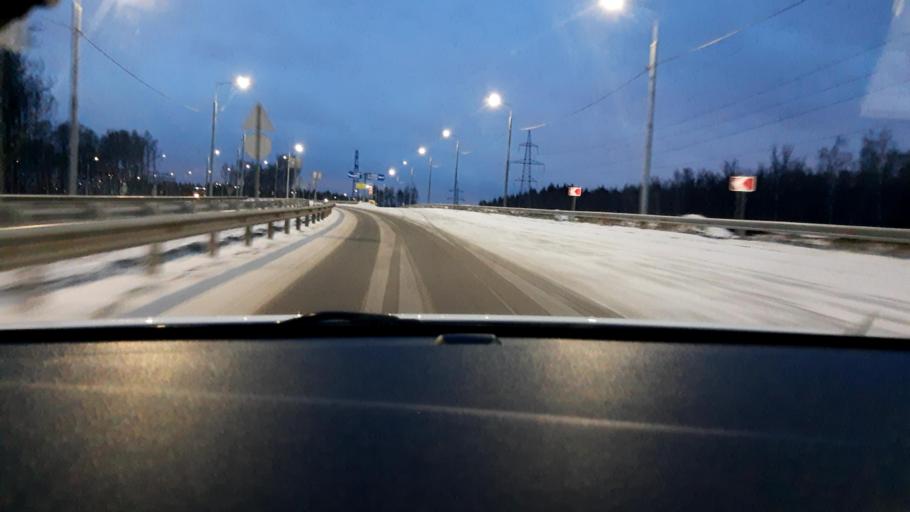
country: RU
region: Moskovskaya
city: Barvikha
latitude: 55.7154
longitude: 37.3119
